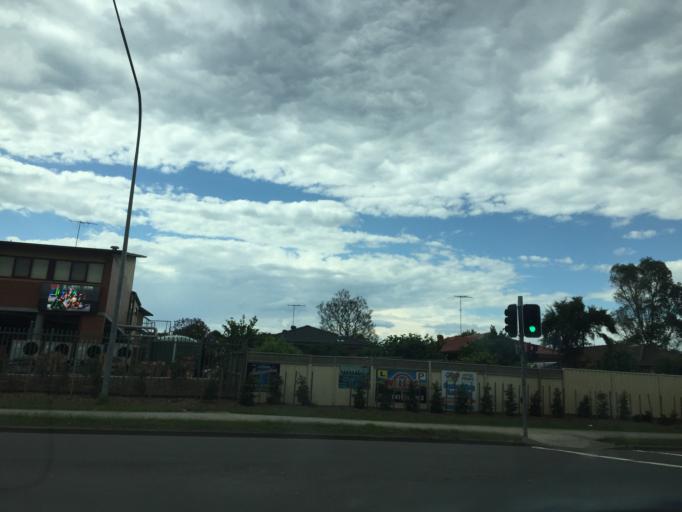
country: AU
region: New South Wales
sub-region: Blacktown
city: Hassall Grove
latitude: -33.7442
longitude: 150.8372
